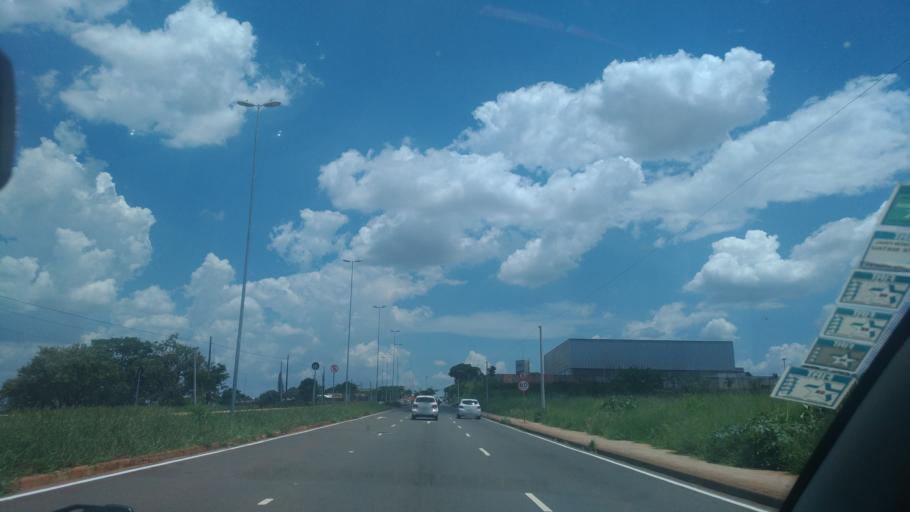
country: BR
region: Sao Paulo
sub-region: Nova Odessa
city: Nova Odessa
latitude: -22.7669
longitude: -47.3177
